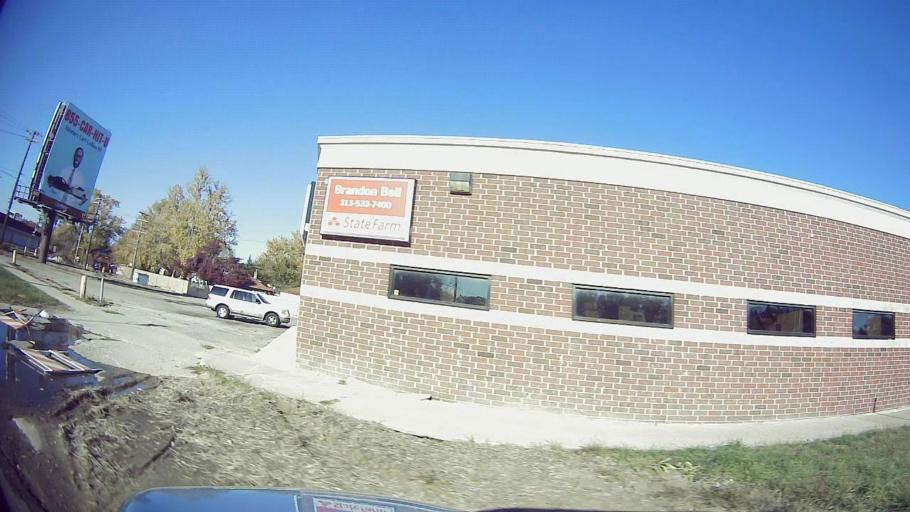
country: US
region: Michigan
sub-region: Wayne County
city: Redford
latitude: 42.4263
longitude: -83.2814
